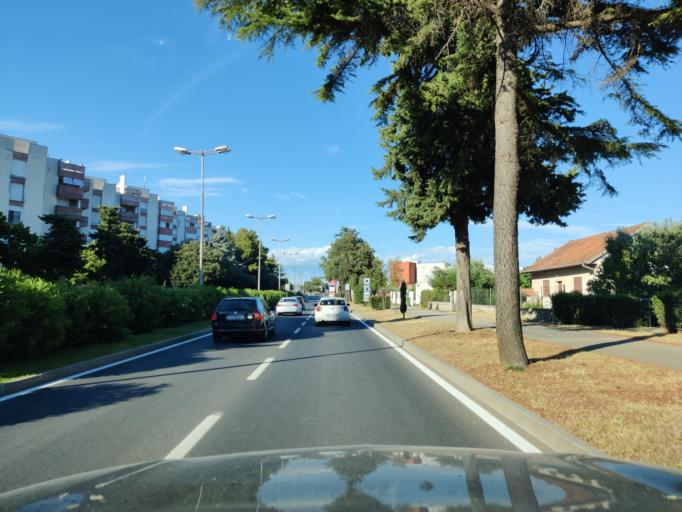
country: HR
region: Zadarska
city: Zadar
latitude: 44.1092
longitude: 15.2461
